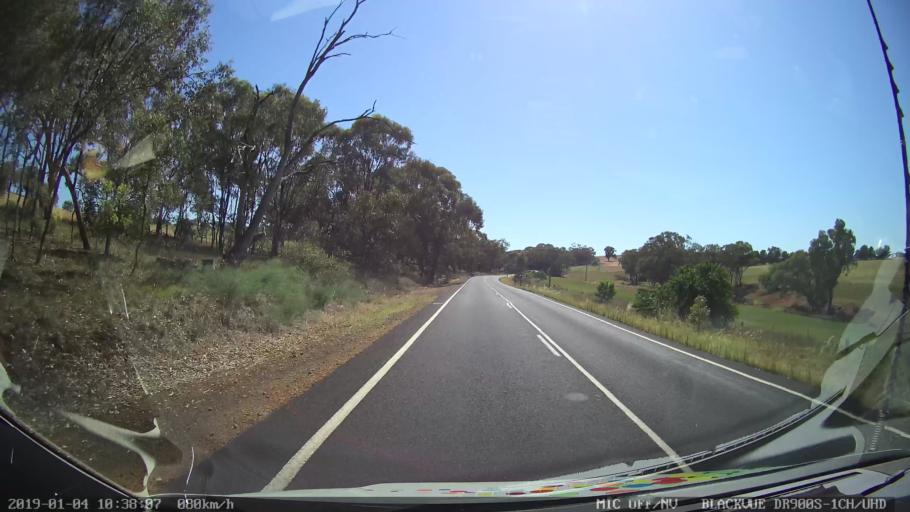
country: AU
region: New South Wales
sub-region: Cabonne
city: Molong
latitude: -33.2942
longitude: 148.7044
